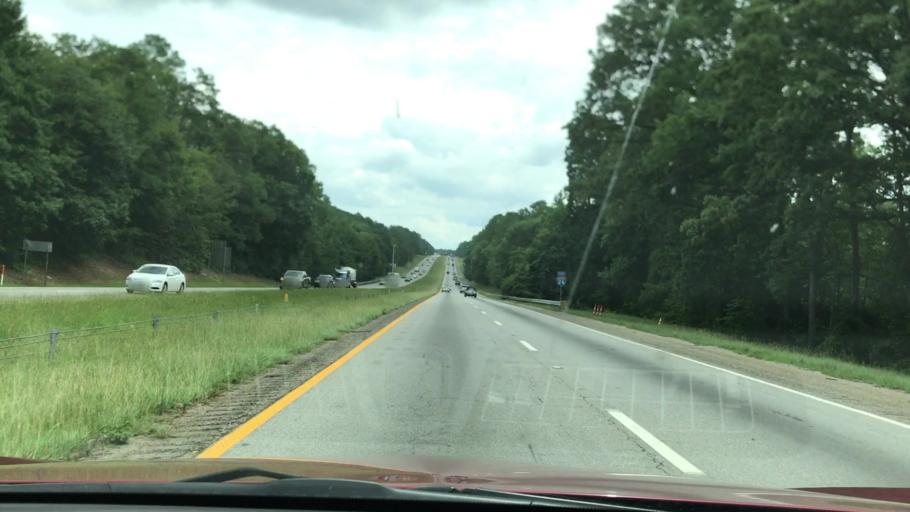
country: US
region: South Carolina
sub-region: Richland County
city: Lake Murray of Richland
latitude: 34.1434
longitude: -81.2324
